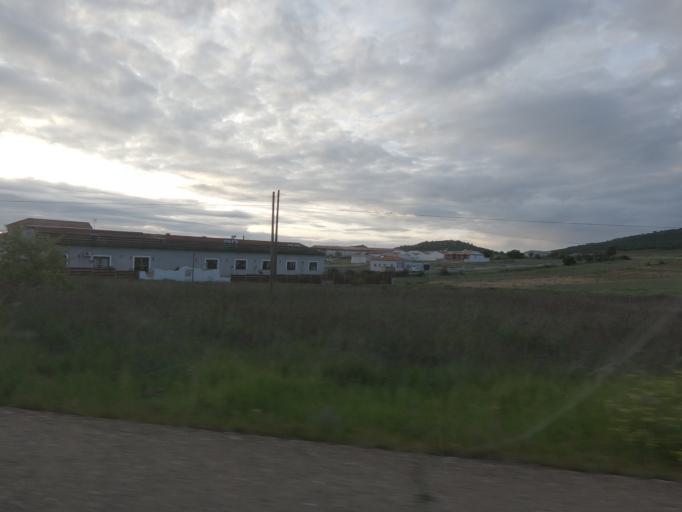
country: ES
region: Extremadura
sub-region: Provincia de Badajoz
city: Puebla de Obando
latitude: 39.1760
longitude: -6.6197
